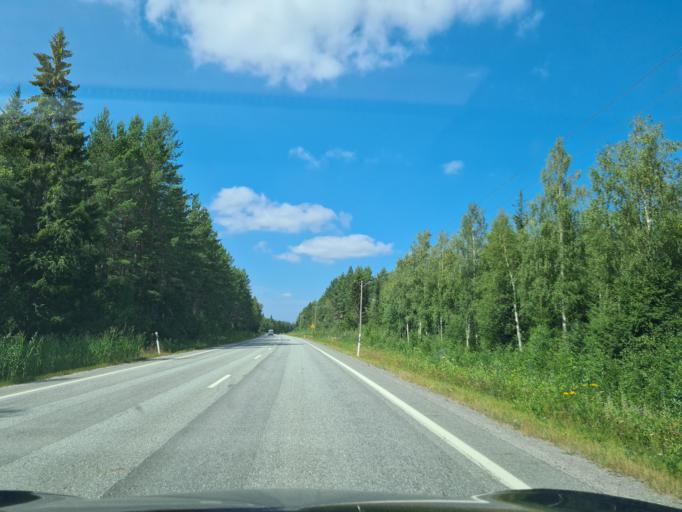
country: FI
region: Ostrobothnia
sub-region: Vaasa
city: Vaasa
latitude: 63.1796
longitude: 21.5740
